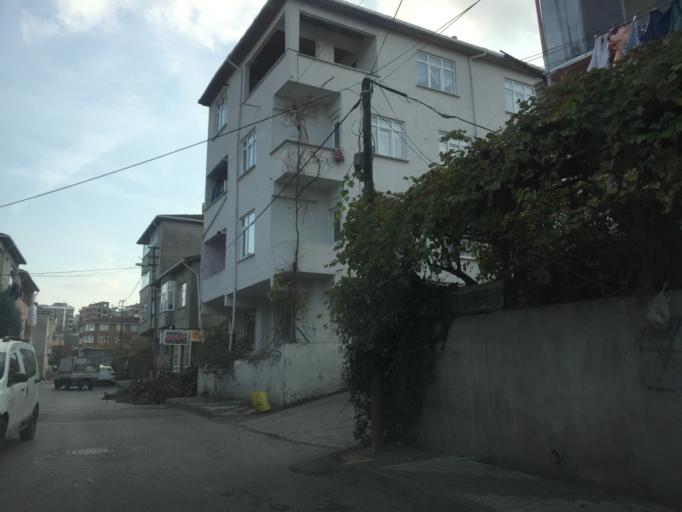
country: TR
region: Istanbul
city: Sultanbeyli
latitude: 40.9446
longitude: 29.2977
